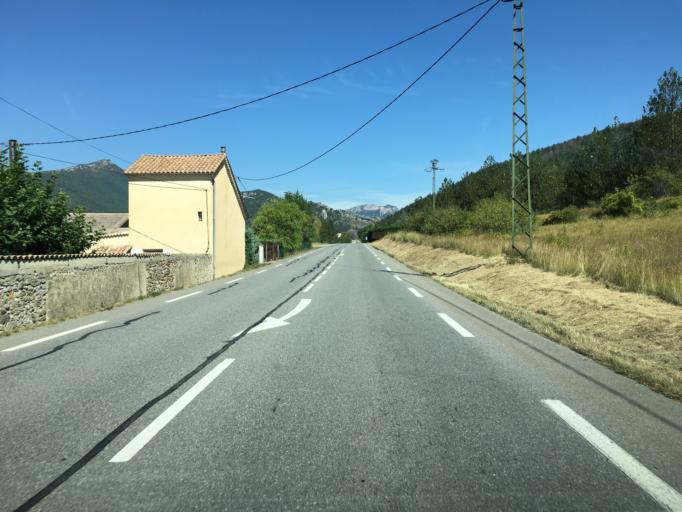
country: FR
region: Provence-Alpes-Cote d'Azur
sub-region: Departement des Hautes-Alpes
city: Serres
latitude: 44.4123
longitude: 5.7251
